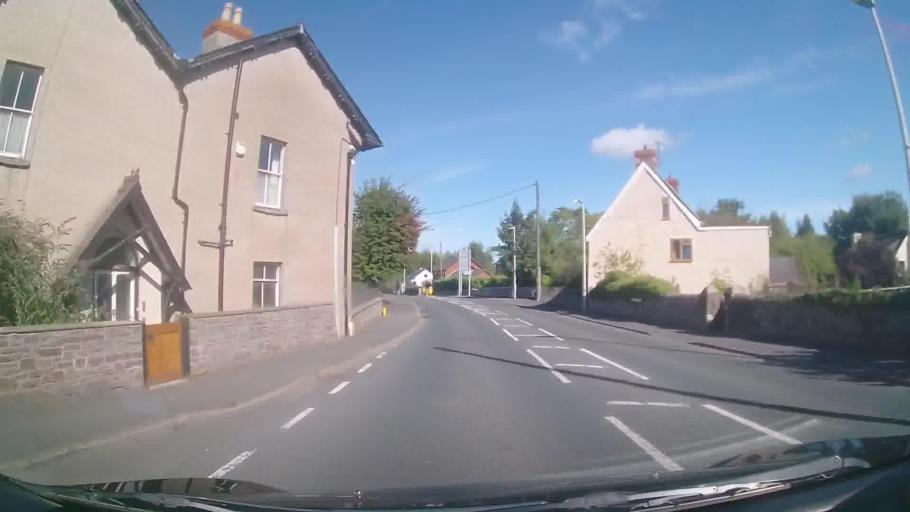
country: GB
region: Wales
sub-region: Sir Powys
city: Hay
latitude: 51.9982
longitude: -3.2337
